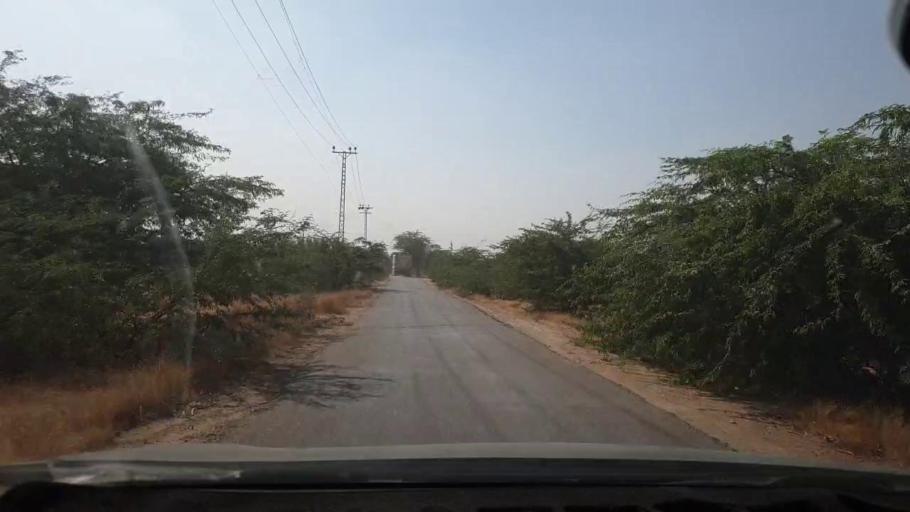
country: PK
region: Sindh
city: Malir Cantonment
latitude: 25.0969
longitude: 67.1883
